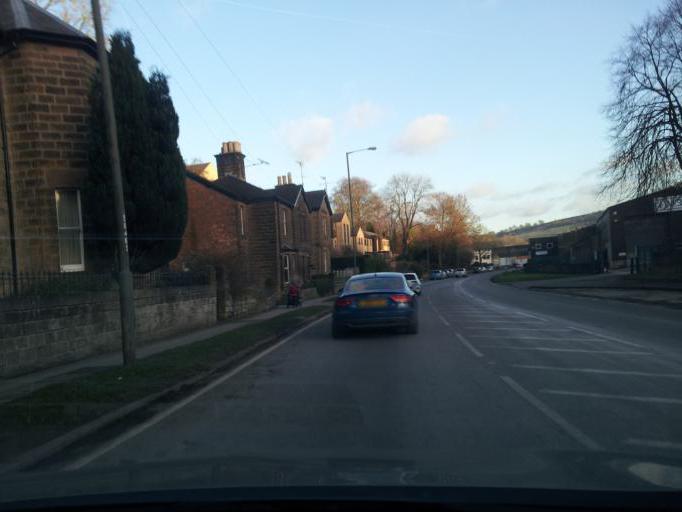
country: GB
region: England
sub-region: Derbyshire
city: Matlock
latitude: 53.1408
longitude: -1.5616
